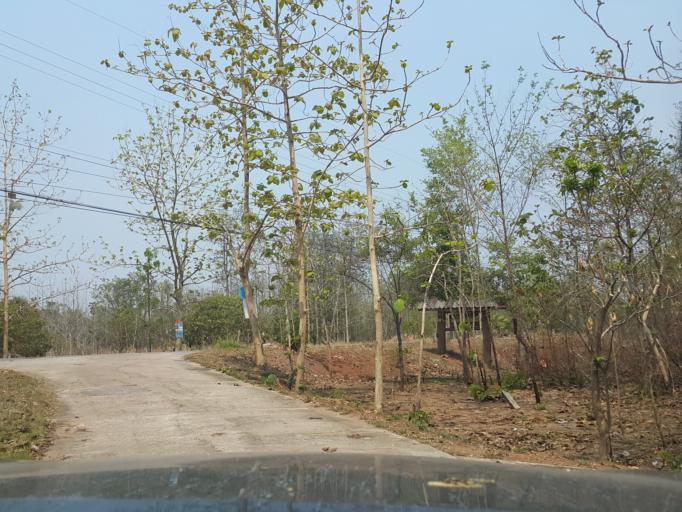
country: TH
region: Lampang
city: Mae Phrik
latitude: 17.5653
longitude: 99.0914
